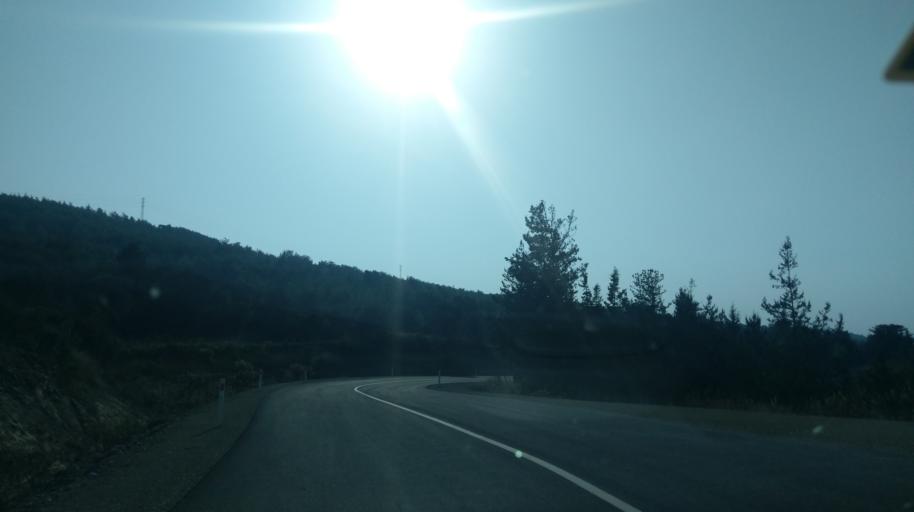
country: CY
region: Ammochostos
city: Leonarisso
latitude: 35.5360
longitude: 34.2343
